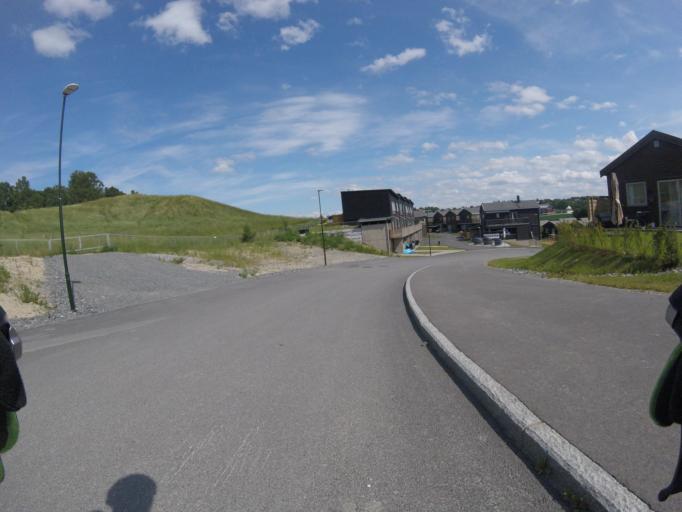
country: NO
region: Akershus
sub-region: Skedsmo
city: Lillestrom
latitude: 59.9782
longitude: 11.0376
